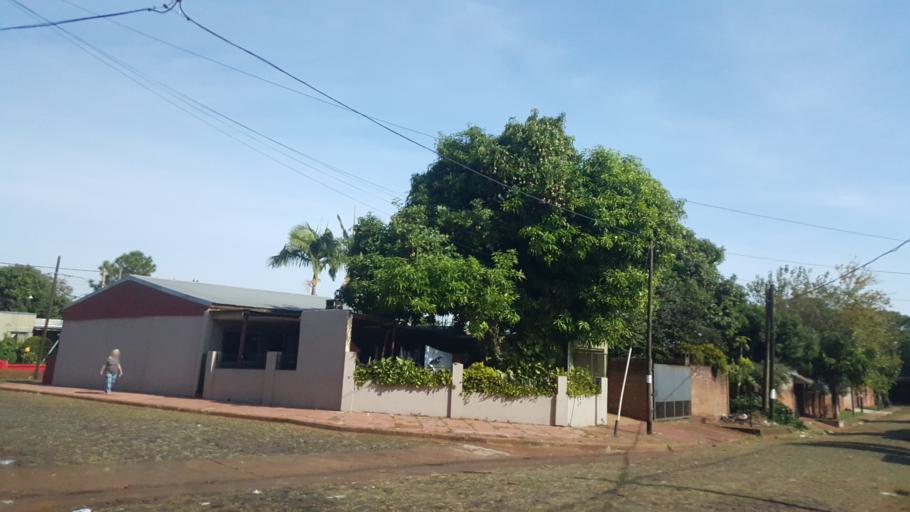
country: AR
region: Misiones
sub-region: Departamento de Capital
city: Posadas
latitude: -27.3868
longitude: -55.9164
